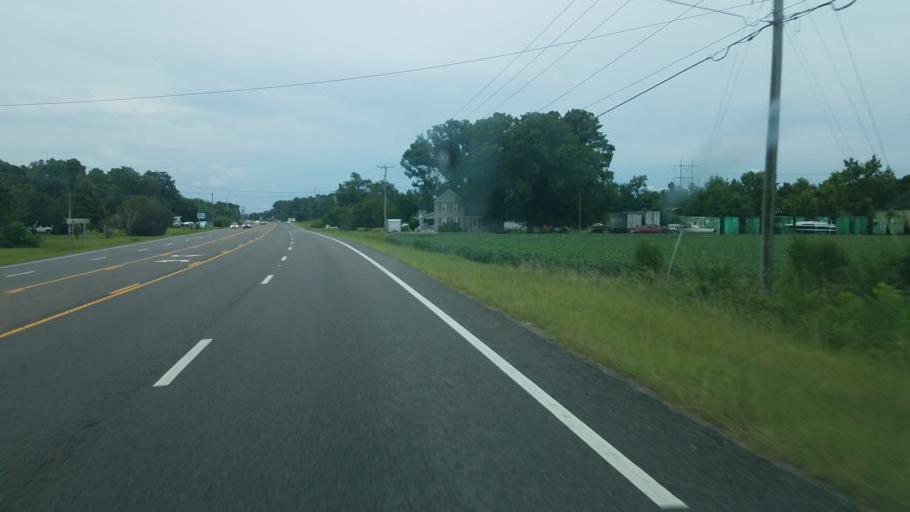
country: US
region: North Carolina
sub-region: Dare County
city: Southern Shores
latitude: 36.1288
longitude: -75.8375
